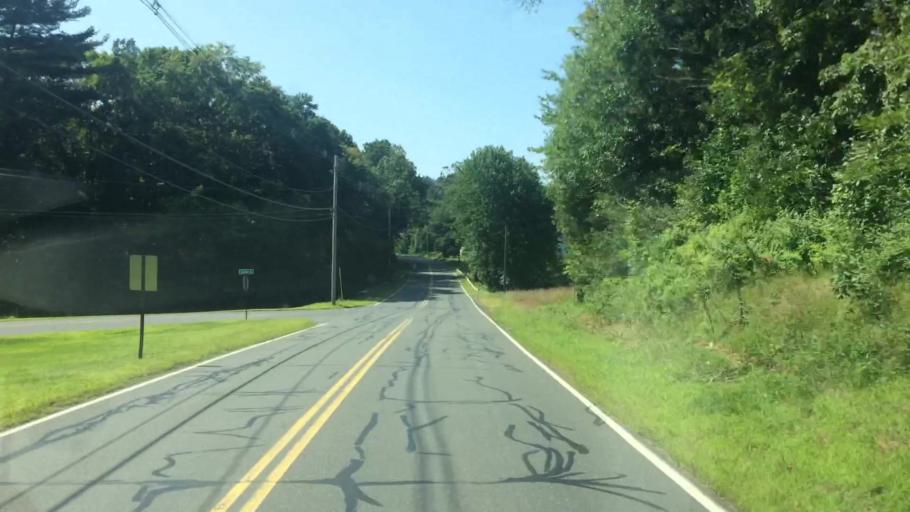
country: US
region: Massachusetts
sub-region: Hampshire County
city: Granby
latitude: 42.2733
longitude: -72.5318
